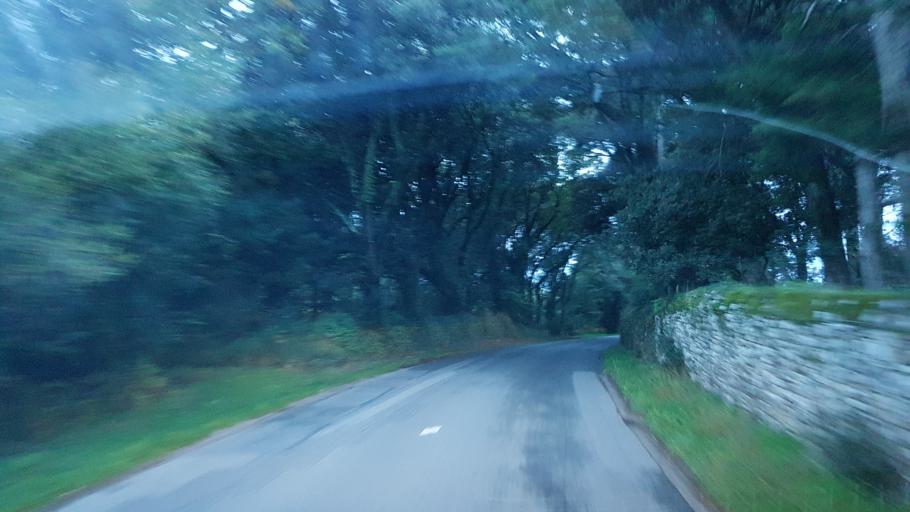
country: FR
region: Brittany
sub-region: Departement du Morbihan
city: Sarzeau
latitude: 47.5374
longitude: -2.7802
